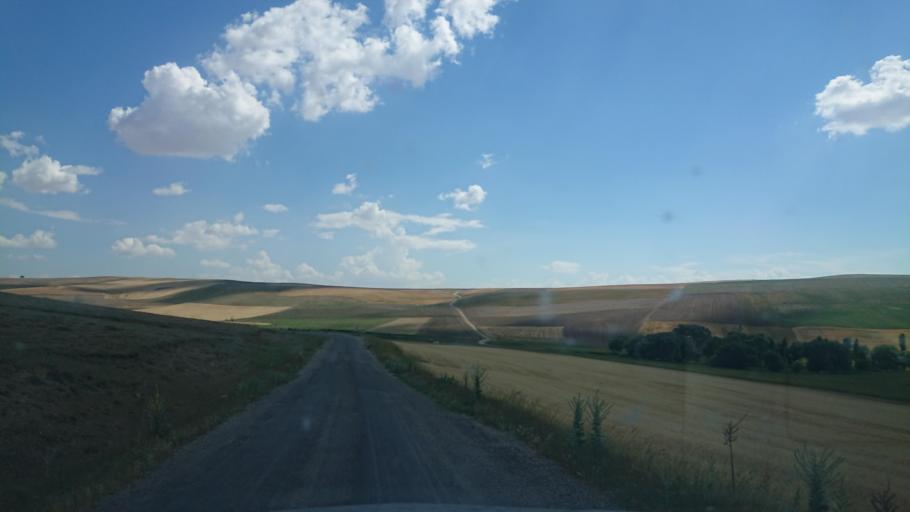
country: TR
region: Aksaray
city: Agacoren
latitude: 38.8240
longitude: 33.7905
